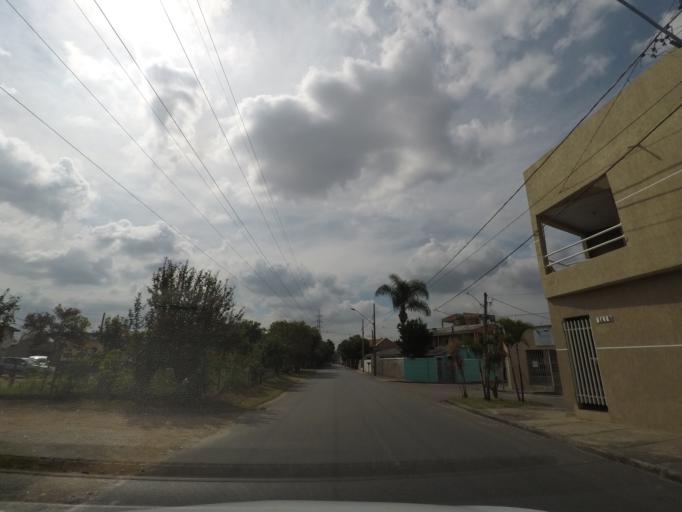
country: BR
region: Parana
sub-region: Pinhais
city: Pinhais
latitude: -25.4656
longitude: -49.1968
